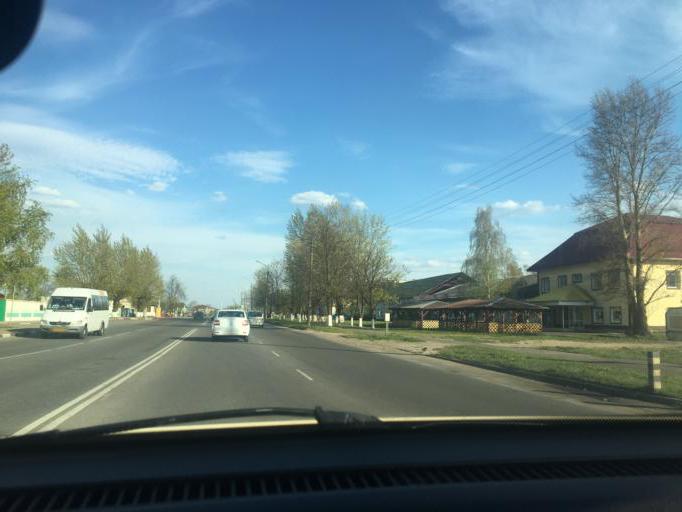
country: BY
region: Mogilev
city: Babruysk
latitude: 53.1496
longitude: 29.1895
